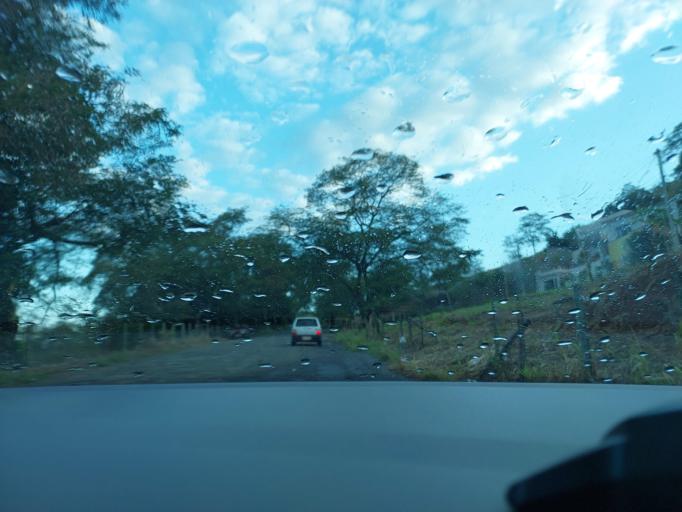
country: BR
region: Rio de Janeiro
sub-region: Natividade
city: Natividade
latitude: -21.1857
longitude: -42.1044
